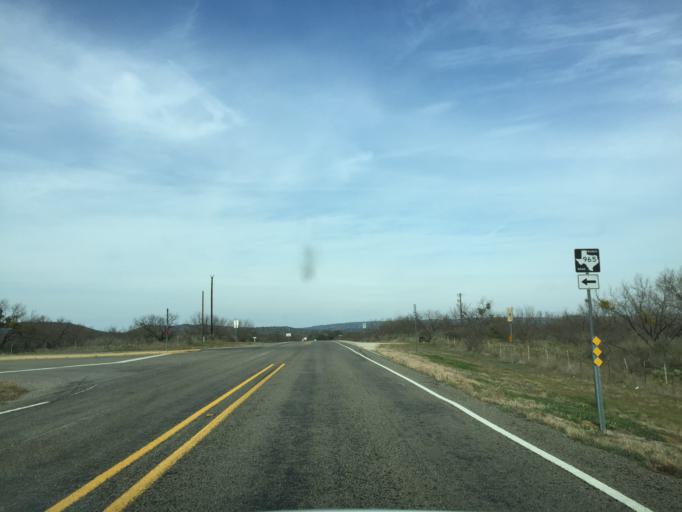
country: US
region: Texas
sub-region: Llano County
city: Llano
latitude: 30.5426
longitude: -98.7046
